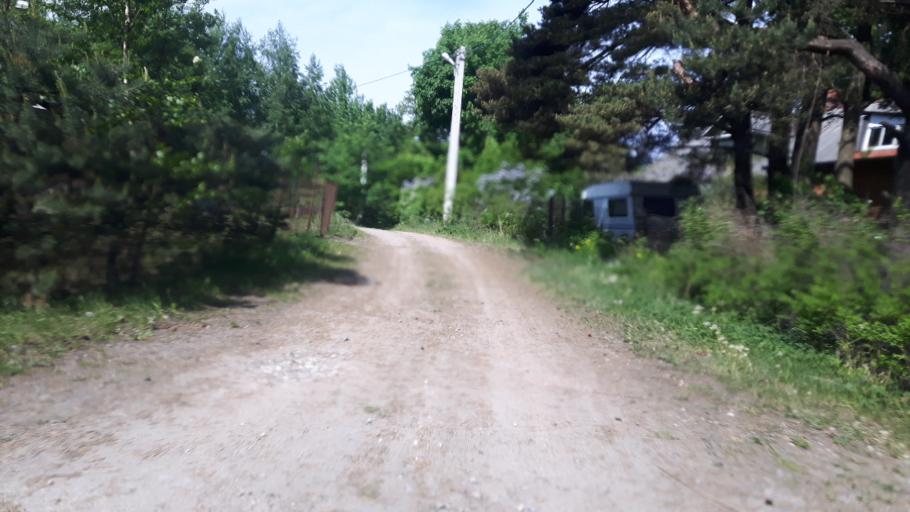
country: RU
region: Leningrad
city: Vistino
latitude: 59.6753
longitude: 28.4406
